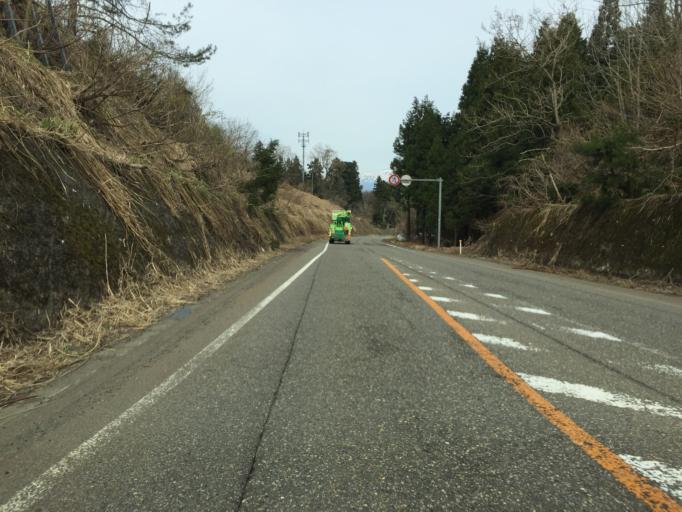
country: JP
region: Niigata
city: Tochio-honcho
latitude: 37.4511
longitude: 138.9537
